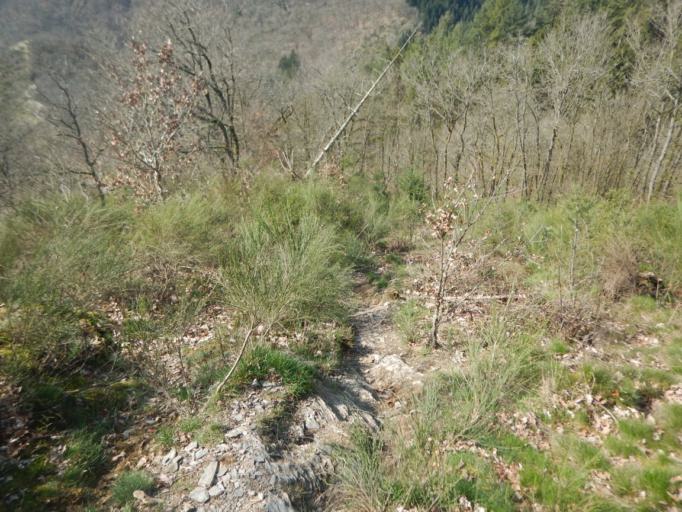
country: LU
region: Diekirch
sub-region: Canton de Diekirch
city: Bourscheid
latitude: 49.9492
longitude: 6.0699
